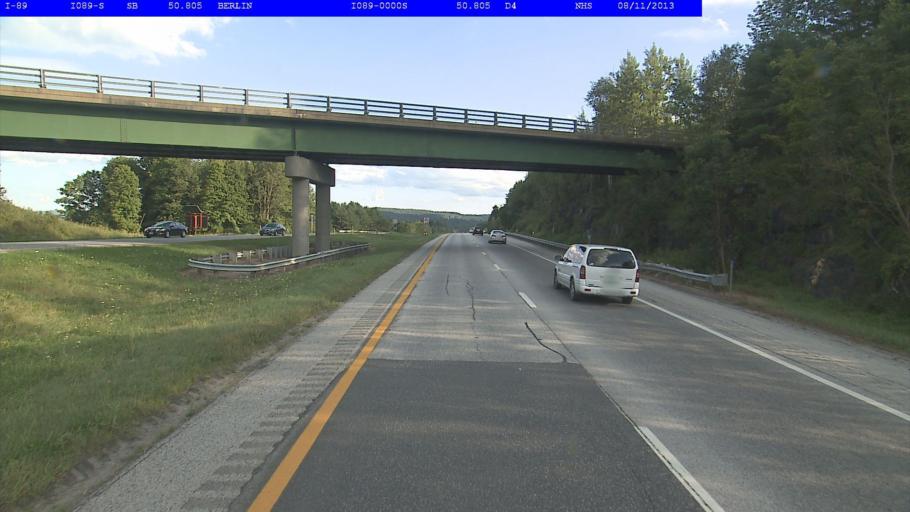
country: US
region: Vermont
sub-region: Washington County
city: Montpelier
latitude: 44.2230
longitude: -72.5855
